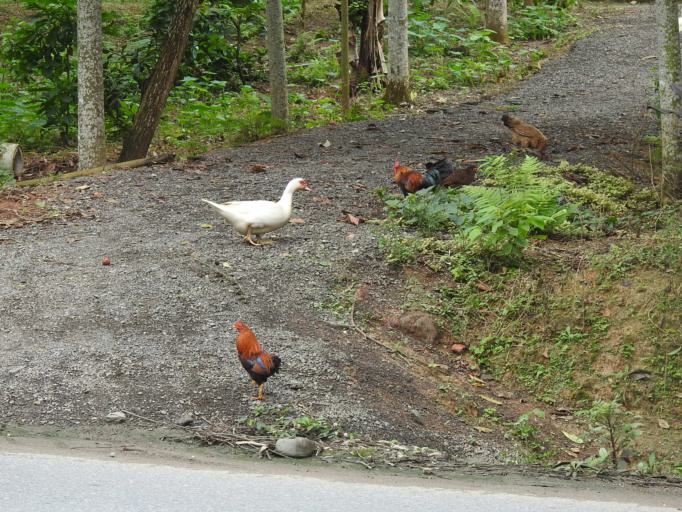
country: VN
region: Phu Tho
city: Thanh Ba
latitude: 21.5109
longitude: 105.2126
